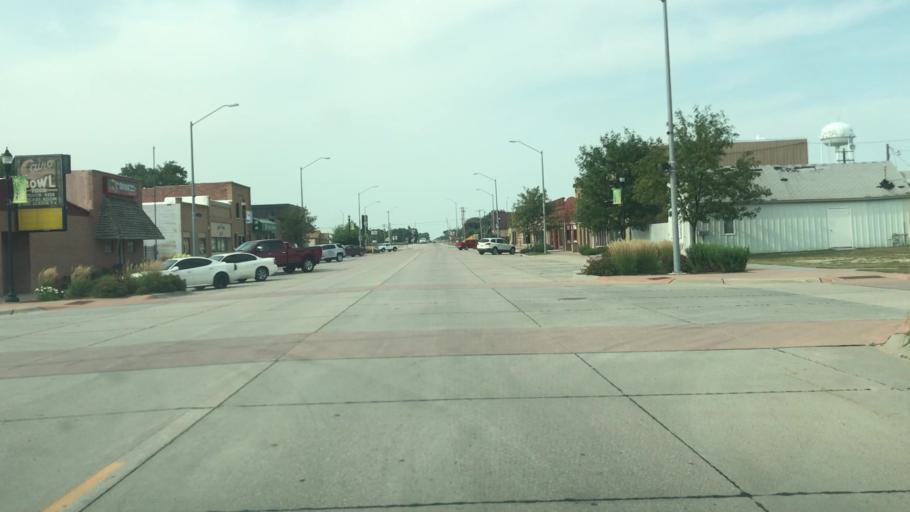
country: US
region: Nebraska
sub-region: Hall County
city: Wood River
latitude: 40.9998
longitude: -98.6074
